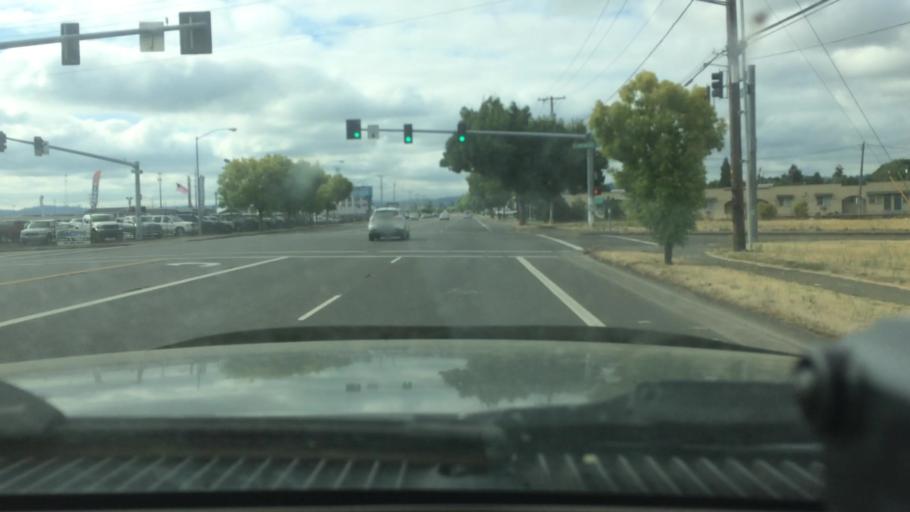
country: US
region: Oregon
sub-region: Lane County
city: Eugene
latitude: 44.0807
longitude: -123.1519
